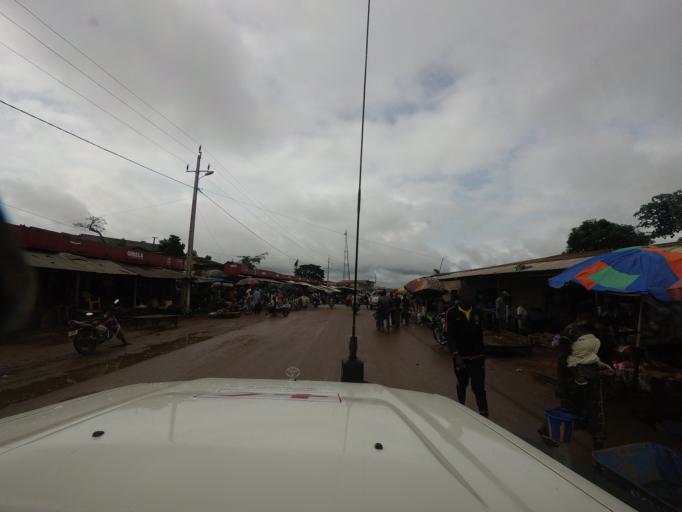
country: GN
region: Nzerekore
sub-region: Nzerekore Prefecture
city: Nzerekore
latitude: 7.7506
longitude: -8.8220
